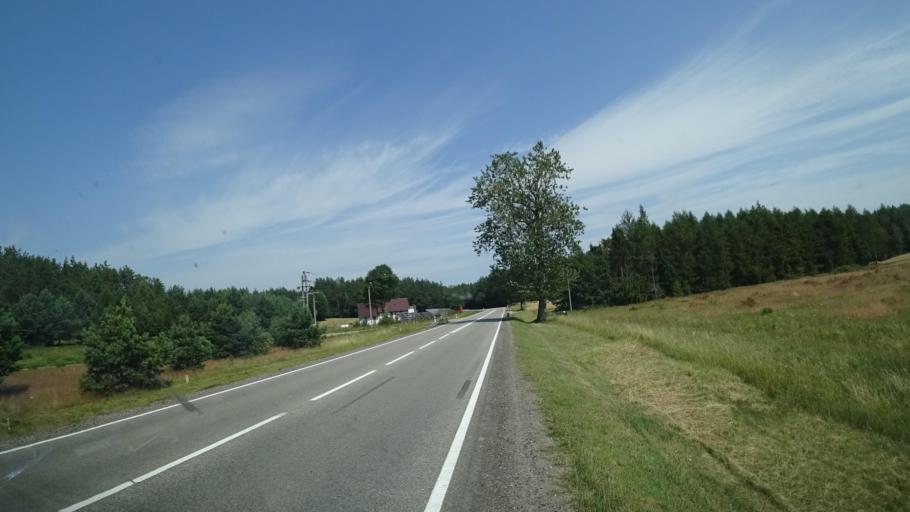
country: PL
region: Pomeranian Voivodeship
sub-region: Powiat koscierski
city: Grabowo Koscierskie
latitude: 54.1872
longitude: 18.1031
